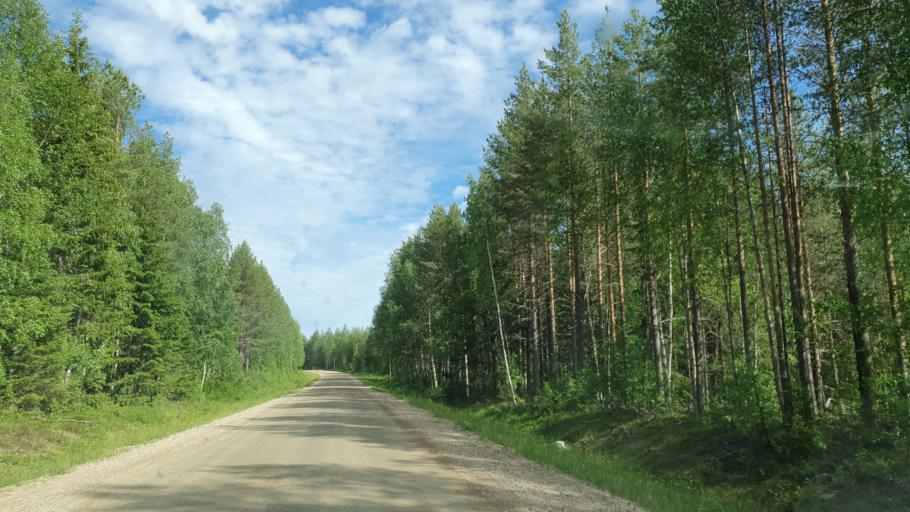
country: FI
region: Kainuu
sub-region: Kehys-Kainuu
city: Kuhmo
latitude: 64.5135
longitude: 29.4269
